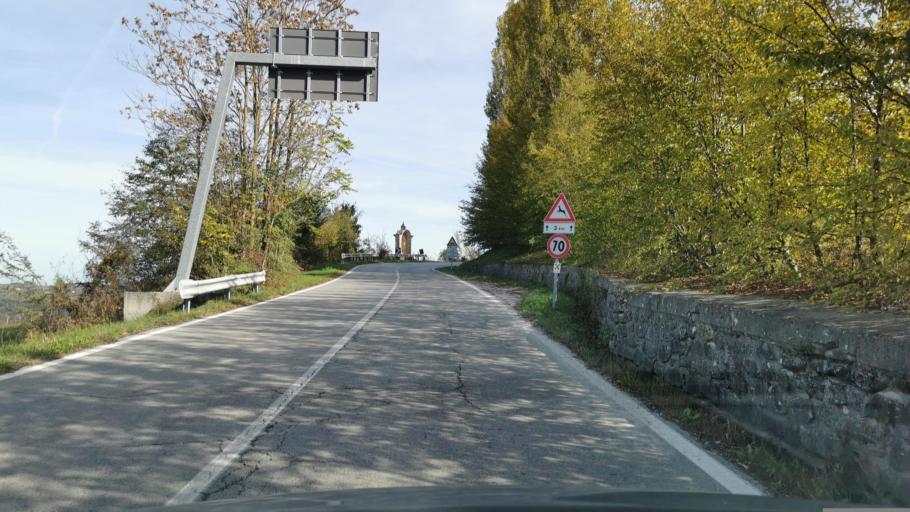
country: IT
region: Piedmont
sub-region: Provincia di Cuneo
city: Dogliani
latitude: 44.5223
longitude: 7.9457
